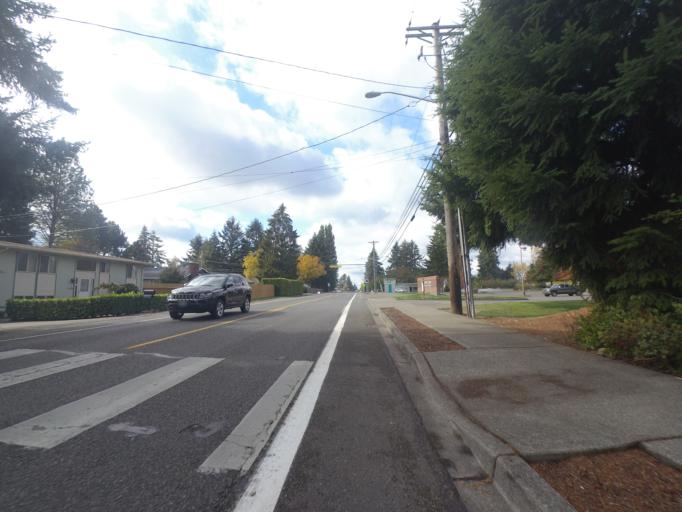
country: US
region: Washington
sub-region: Pierce County
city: University Place
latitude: 47.2172
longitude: -122.5409
